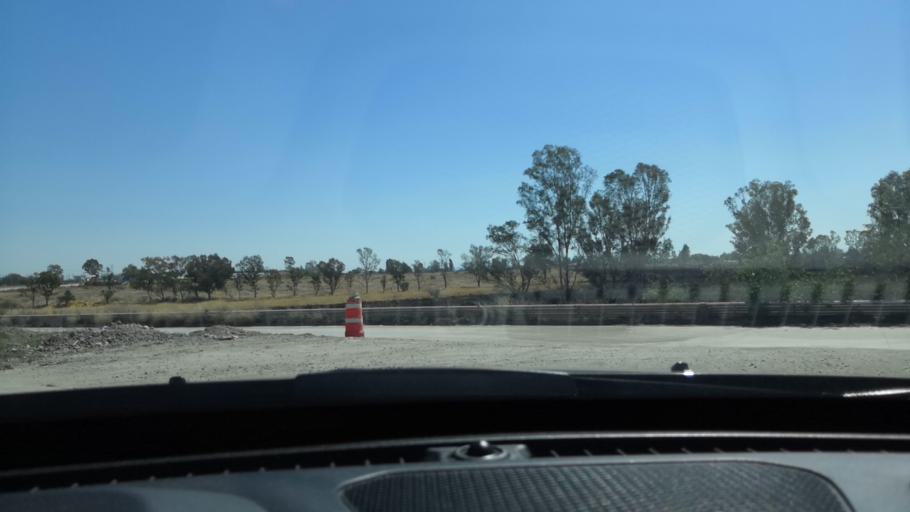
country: MX
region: Guanajuato
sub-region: Leon
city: Centro Familiar la Soledad
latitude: 21.0977
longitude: -101.7819
